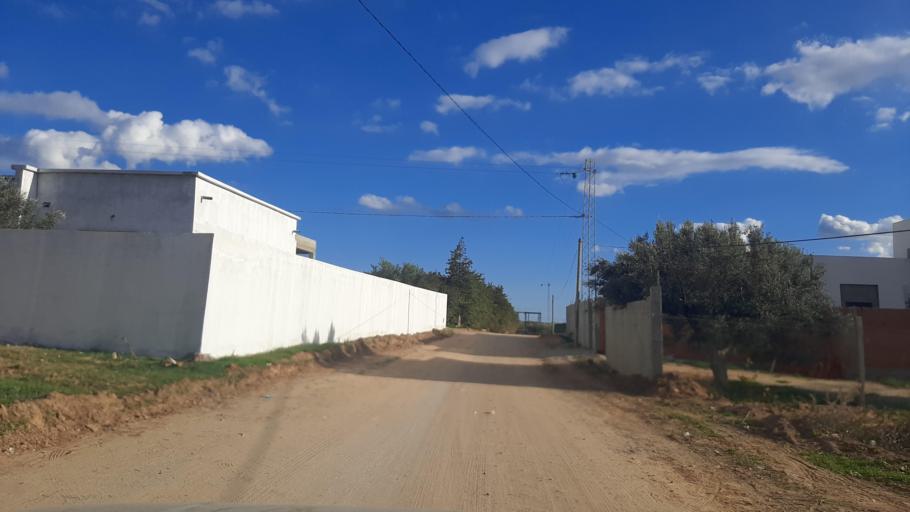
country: TN
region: Nabul
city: Al Hammamat
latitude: 36.4212
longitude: 10.5102
